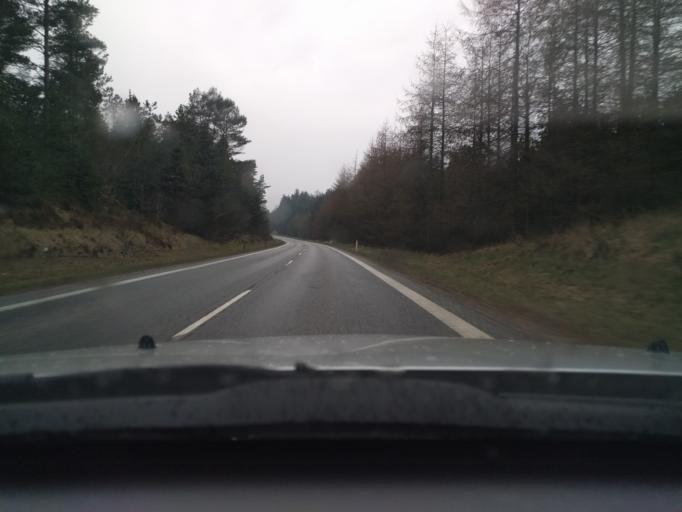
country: DK
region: Central Jutland
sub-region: Viborg Kommune
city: Viborg
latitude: 56.3860
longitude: 9.3003
